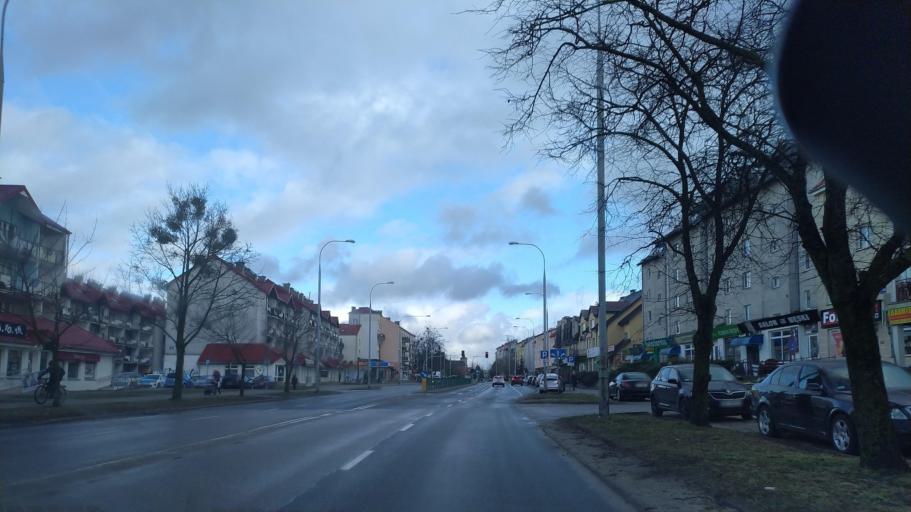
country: PL
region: Warmian-Masurian Voivodeship
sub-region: Powiat olsztynski
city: Olsztyn
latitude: 53.7417
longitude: 20.4993
